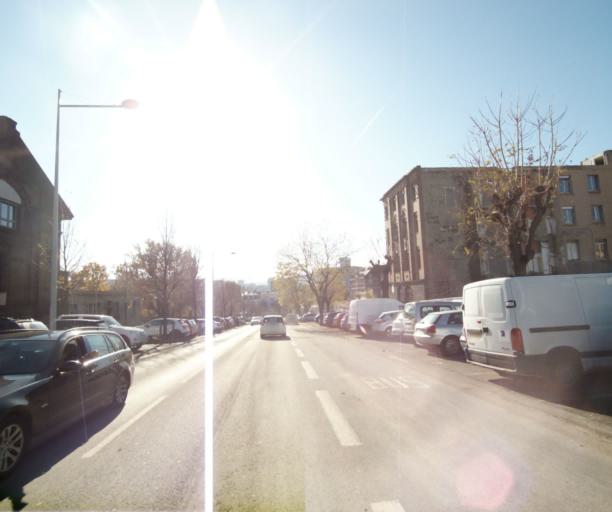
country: FR
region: Auvergne
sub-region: Departement du Puy-de-Dome
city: Clermont-Ferrand
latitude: 45.7727
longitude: 3.0869
